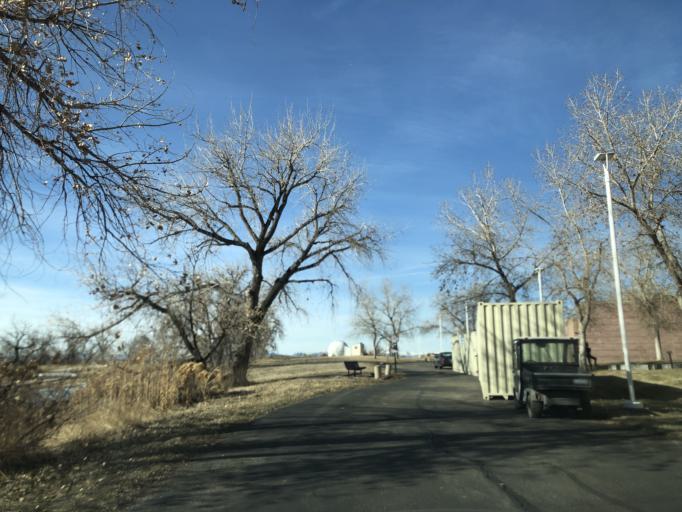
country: US
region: Colorado
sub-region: Adams County
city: Aurora
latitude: 39.7170
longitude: -104.8027
